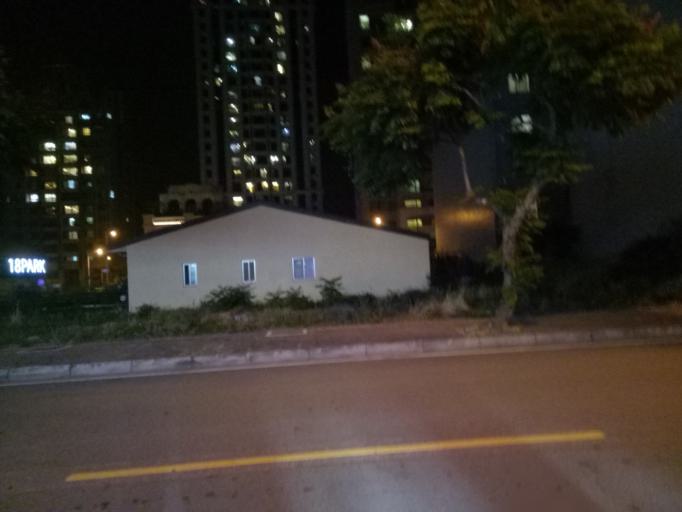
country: TW
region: Taiwan
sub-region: Hsinchu
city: Zhubei
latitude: 24.8260
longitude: 121.0303
